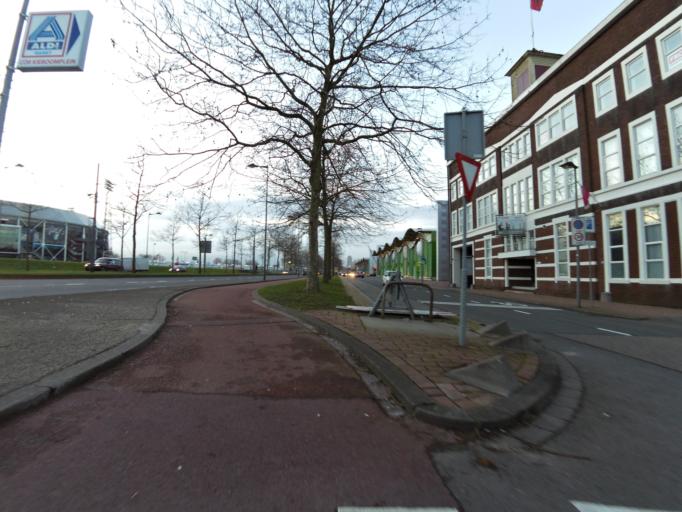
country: NL
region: South Holland
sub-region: Gemeente Rotterdam
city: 's-Gravenland
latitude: 51.8954
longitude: 4.5266
